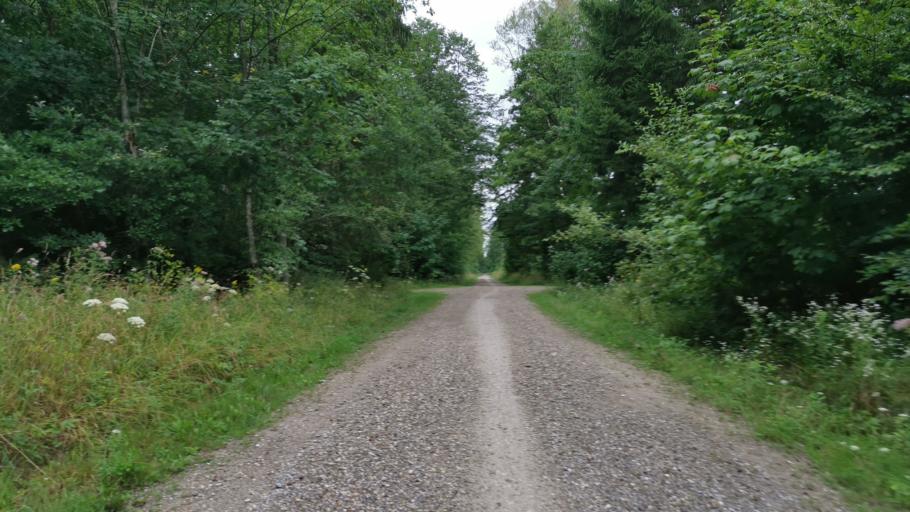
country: DE
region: Bavaria
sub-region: Upper Bavaria
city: Pullach im Isartal
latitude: 48.0726
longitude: 11.5607
